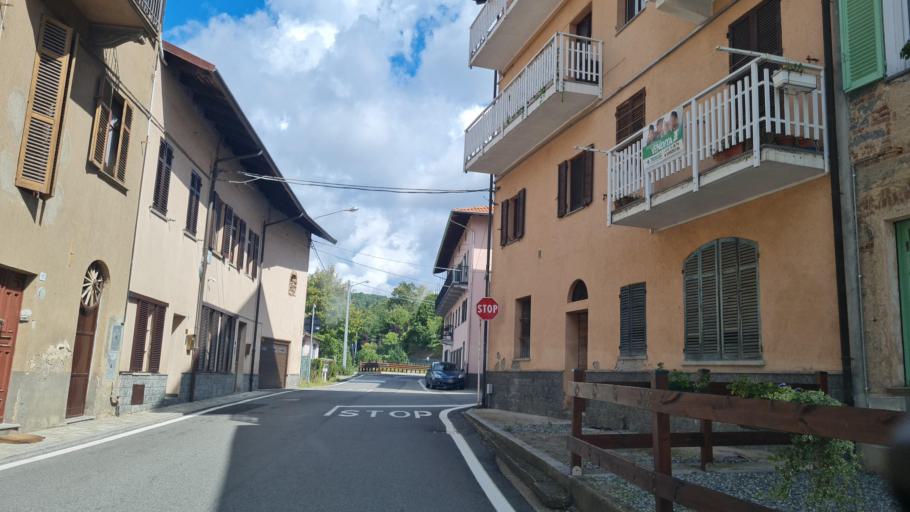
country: IT
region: Piedmont
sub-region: Provincia di Biella
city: Fontanella-Ozino
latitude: 45.6214
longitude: 8.1680
